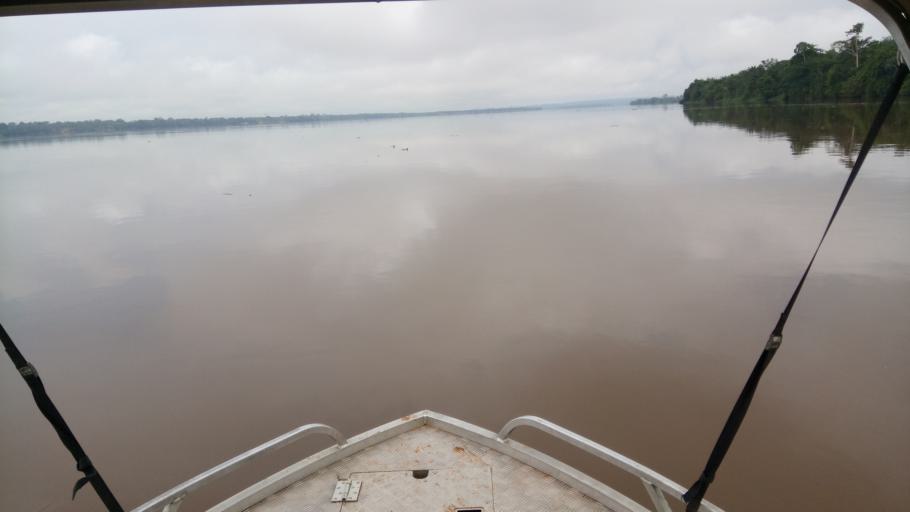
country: CD
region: Eastern Province
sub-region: Sous-Region de la Tshopo
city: Yangambi
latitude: 0.6755
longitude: 24.6040
